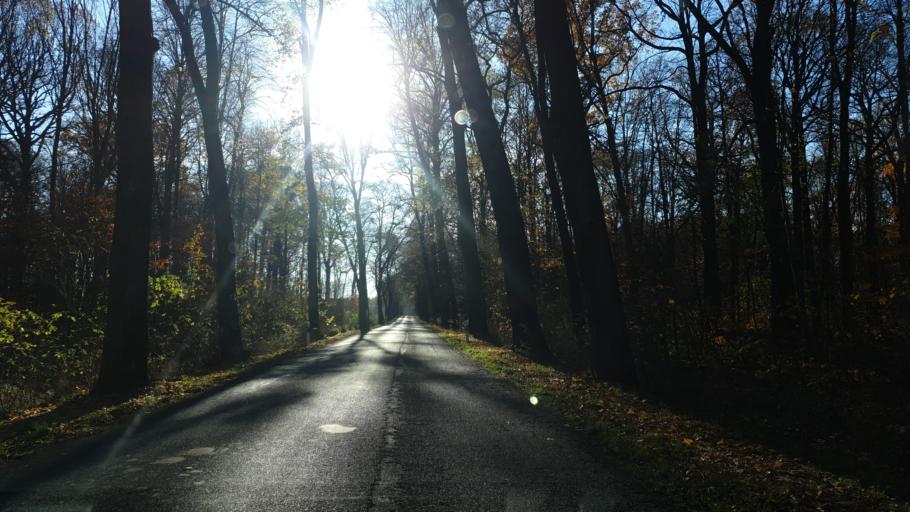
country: DE
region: Saxony-Anhalt
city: Droyssig
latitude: 51.0310
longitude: 12.0215
